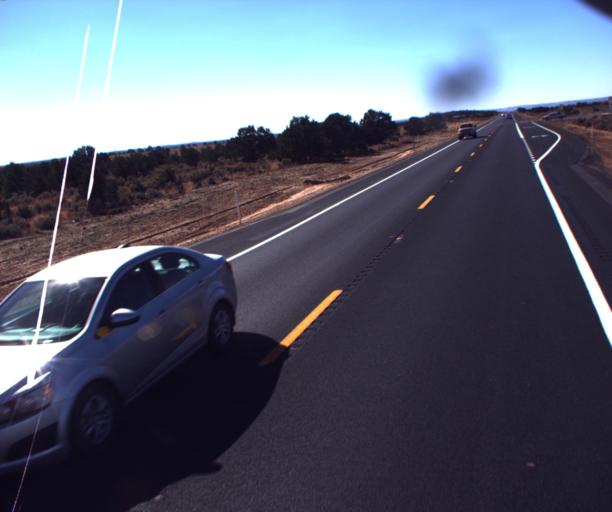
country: US
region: Arizona
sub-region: Apache County
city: Ganado
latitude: 35.7177
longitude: -109.4011
